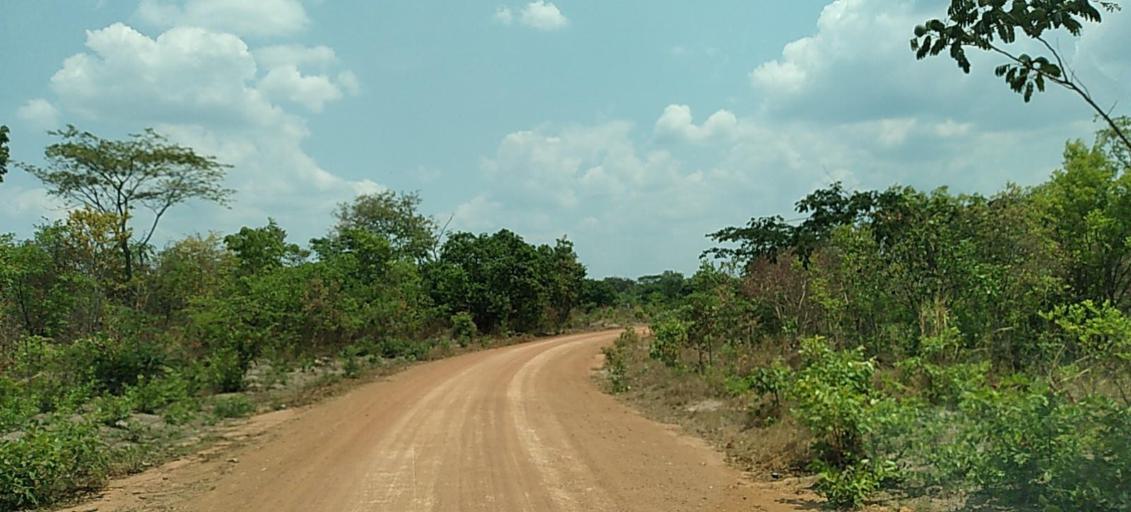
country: ZM
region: Copperbelt
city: Luanshya
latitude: -13.1447
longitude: 28.3169
